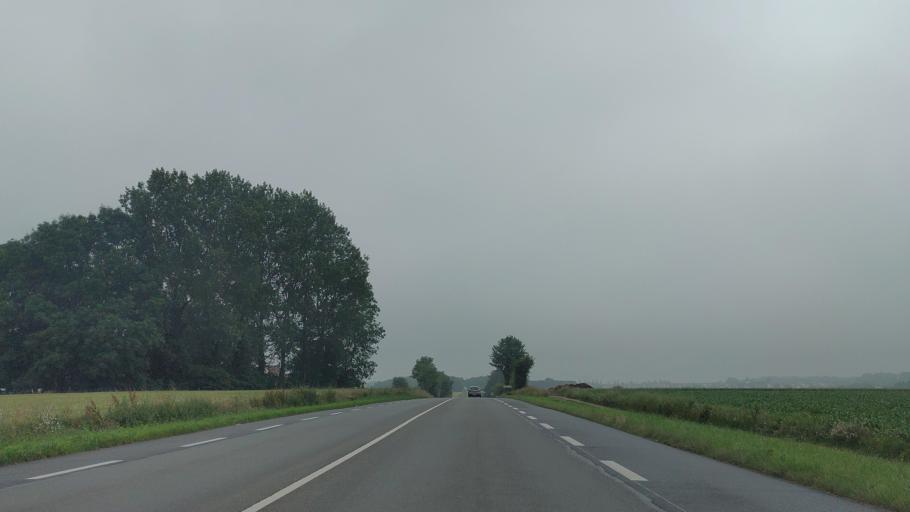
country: FR
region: Picardie
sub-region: Departement de la Somme
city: Fressenneville
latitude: 50.0743
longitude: 1.5759
